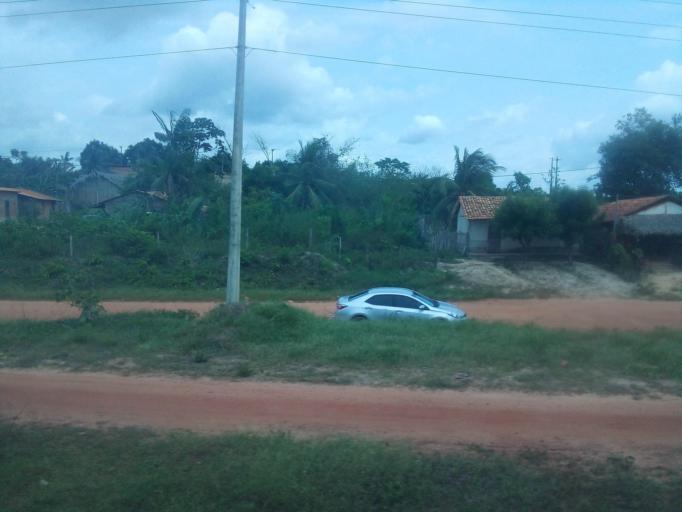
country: BR
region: Maranhao
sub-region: Santa Ines
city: Santa Ines
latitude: -3.7283
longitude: -46.0985
